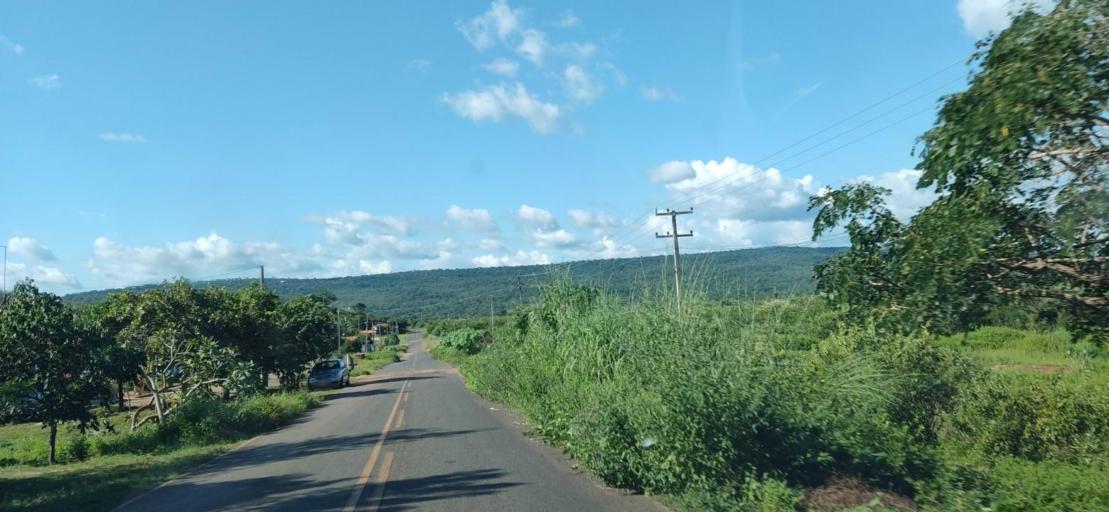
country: BR
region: Piaui
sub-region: Valenca Do Piaui
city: Valenca do Piaui
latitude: -6.1769
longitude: -41.8189
